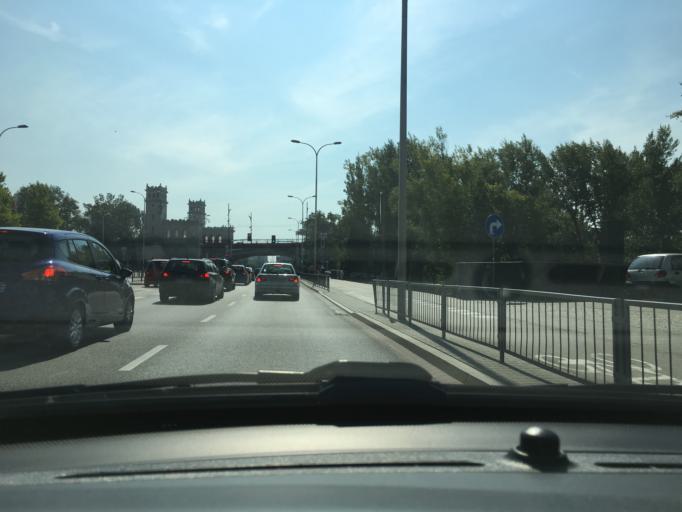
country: PL
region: Masovian Voivodeship
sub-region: Warszawa
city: Praga Polnoc
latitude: 52.2380
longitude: 21.0431
